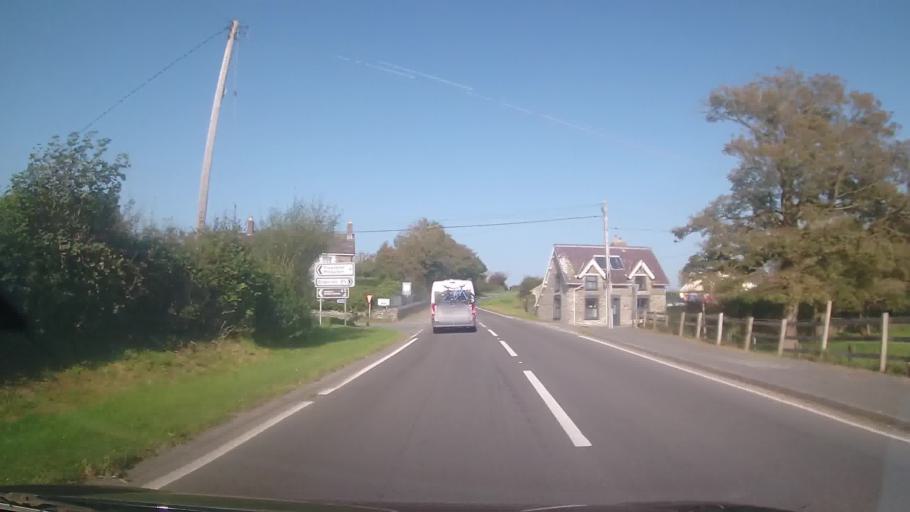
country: GB
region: Wales
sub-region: County of Ceredigion
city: Cardigan
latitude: 52.0538
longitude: -4.6911
